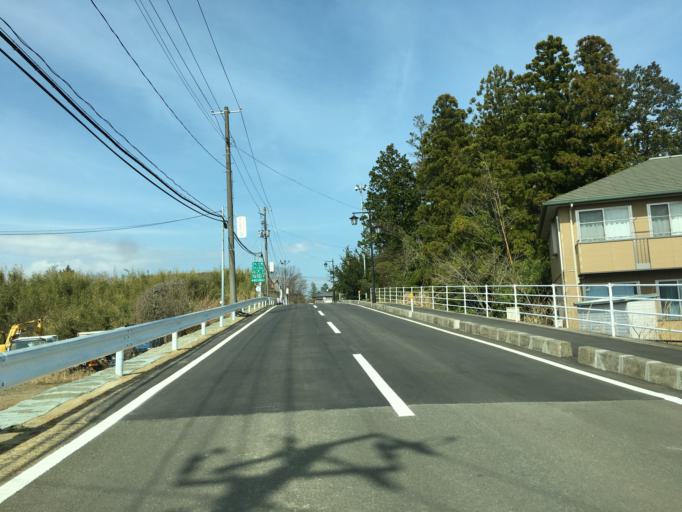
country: JP
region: Fukushima
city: Namie
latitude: 37.4095
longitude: 140.9849
